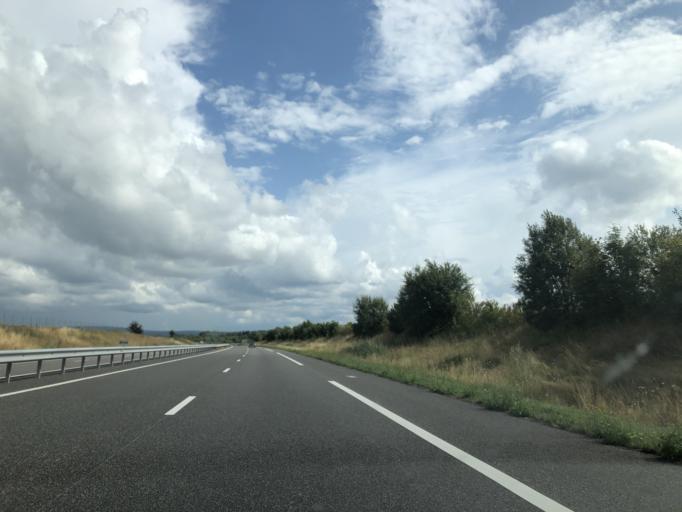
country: FR
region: Lorraine
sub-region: Departement de Meurthe-et-Moselle
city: Baccarat
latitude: 48.4856
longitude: 6.7094
